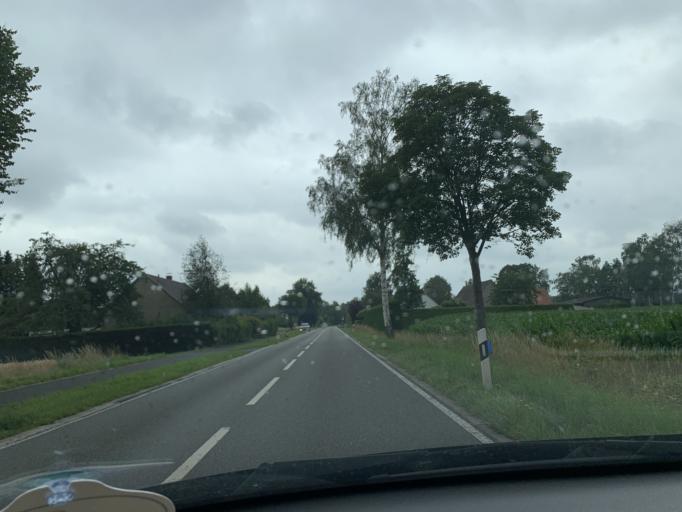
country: DE
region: North Rhine-Westphalia
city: Lengerich
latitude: 52.1633
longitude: 7.8488
